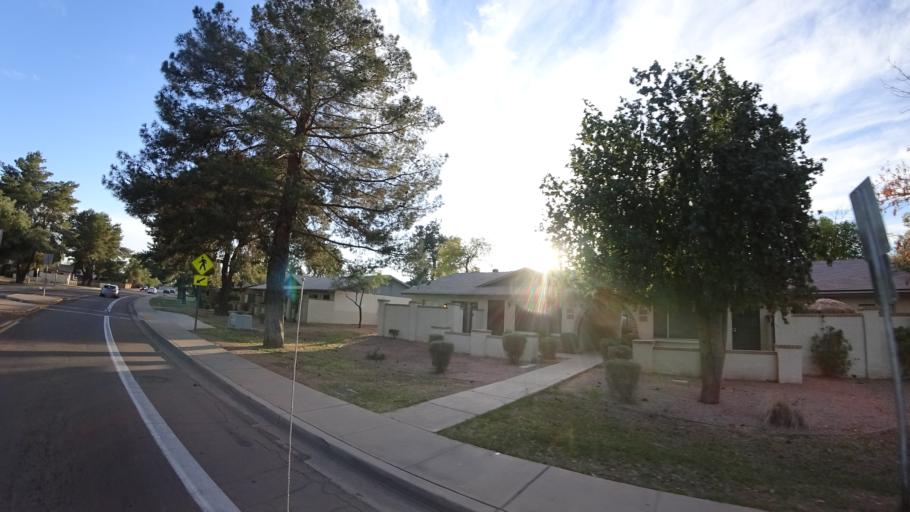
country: US
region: Arizona
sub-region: Maricopa County
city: Guadalupe
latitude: 33.3918
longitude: -111.9520
